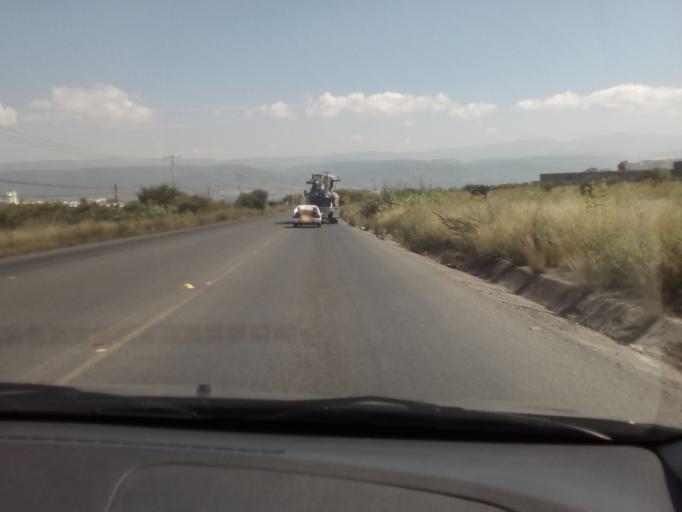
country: MX
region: Guanajuato
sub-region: Leon
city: La Ermita
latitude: 21.1758
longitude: -101.7293
